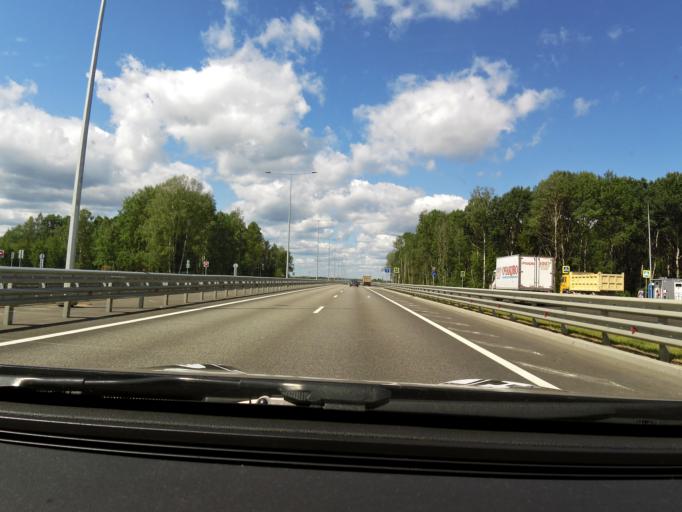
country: RU
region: Tverskaya
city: Vydropuzhsk
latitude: 57.3722
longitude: 34.6239
